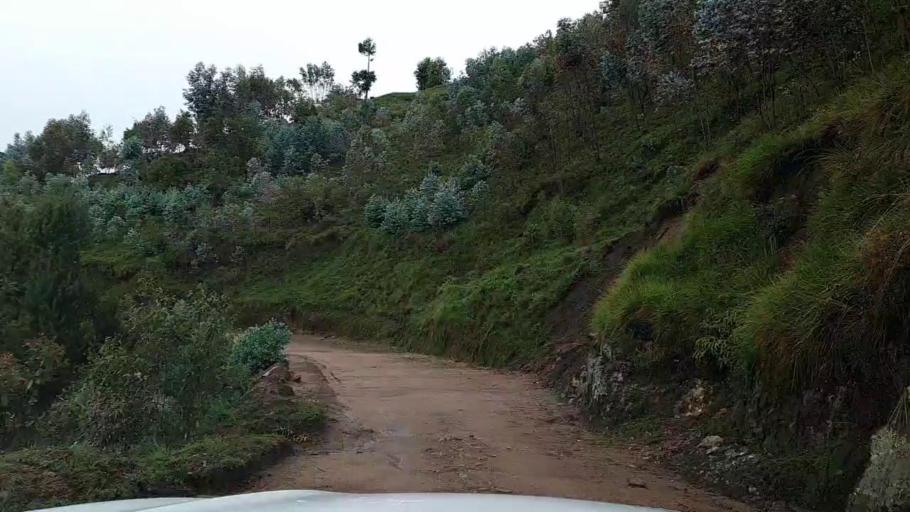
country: RW
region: Southern Province
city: Nzega
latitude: -2.4057
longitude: 29.4932
